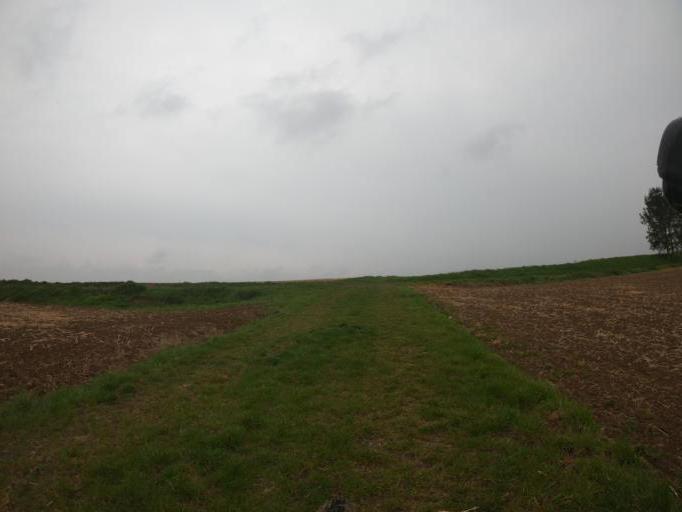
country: DE
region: Baden-Wuerttemberg
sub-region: Regierungsbezirk Stuttgart
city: Hemmingen
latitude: 48.8841
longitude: 9.0246
